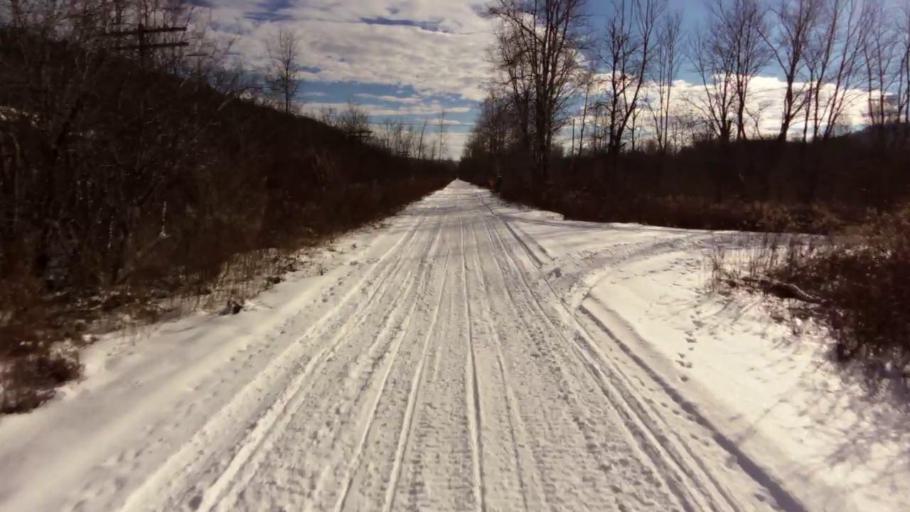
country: US
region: Pennsylvania
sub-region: McKean County
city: Foster Brook
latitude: 42.0181
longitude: -78.6283
